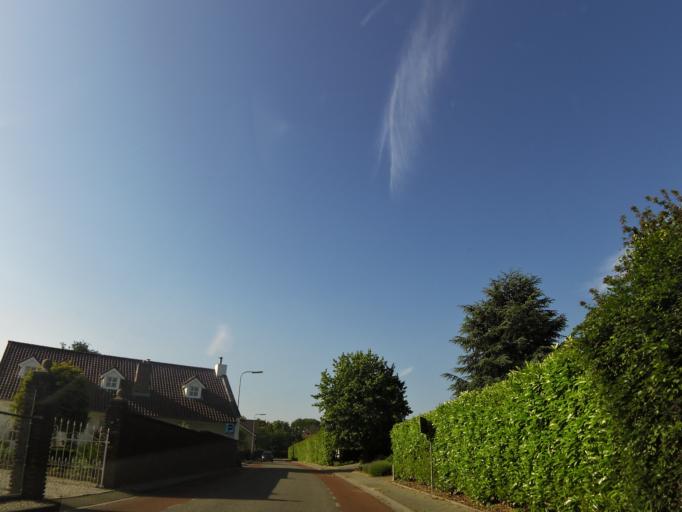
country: NL
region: Limburg
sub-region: Gemeente Beek
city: Beek
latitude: 50.9130
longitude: 5.8107
